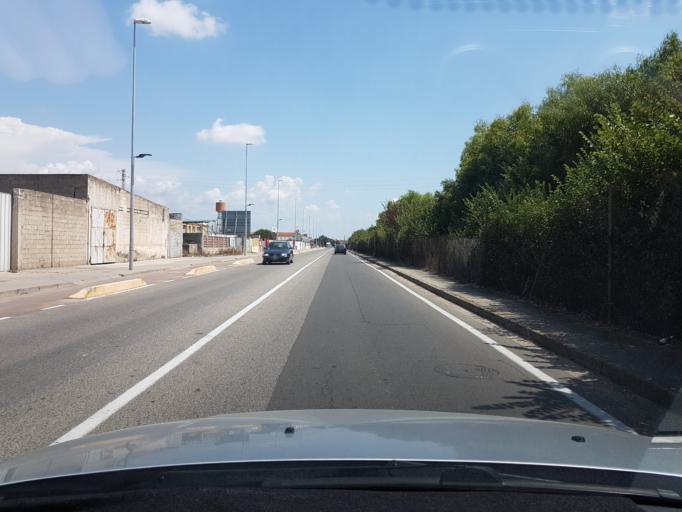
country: IT
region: Sardinia
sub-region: Provincia di Oristano
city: Sili
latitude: 39.9139
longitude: 8.6107
